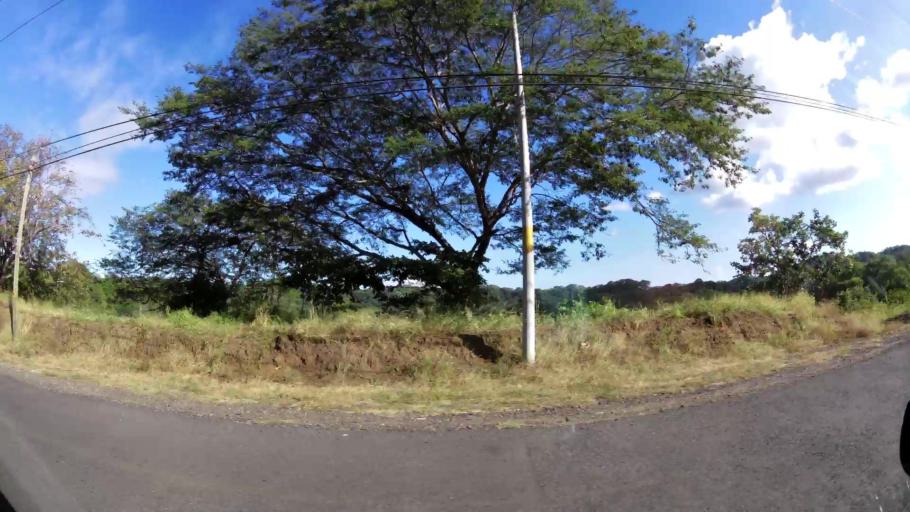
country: CR
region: Guanacaste
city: Sardinal
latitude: 10.5816
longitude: -85.6618
